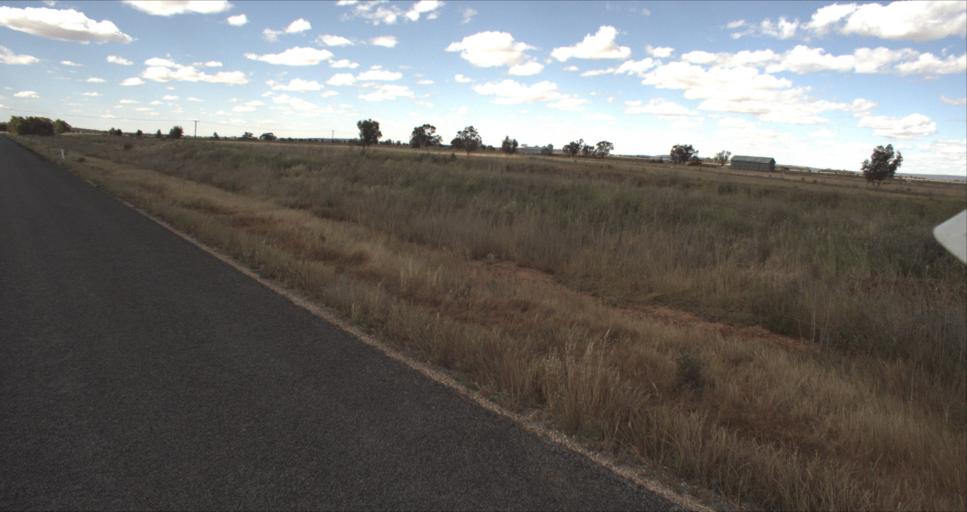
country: AU
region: New South Wales
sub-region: Leeton
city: Leeton
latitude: -34.4485
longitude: 146.2550
